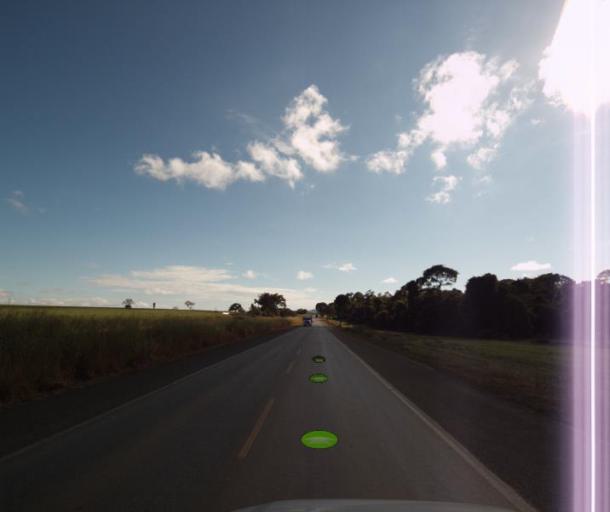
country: BR
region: Goias
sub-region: Uruacu
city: Uruacu
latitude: -14.6503
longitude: -49.1862
